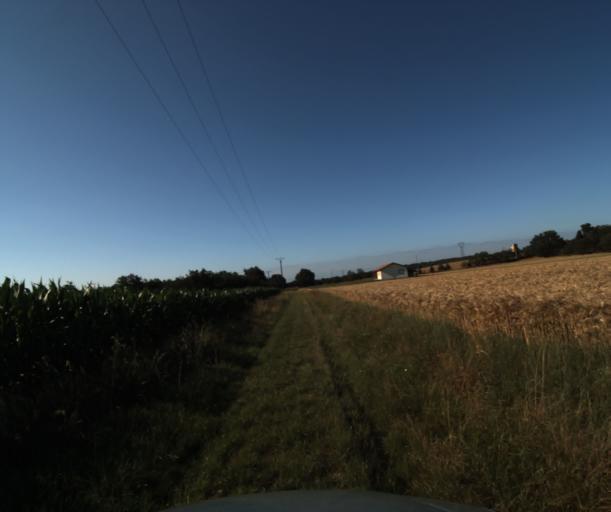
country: FR
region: Midi-Pyrenees
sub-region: Departement de la Haute-Garonne
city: Labarthe-sur-Leze
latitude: 43.4413
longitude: 1.3766
